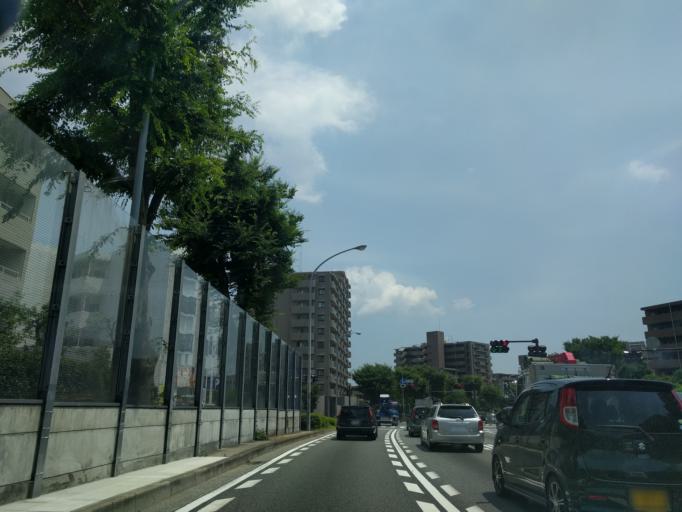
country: JP
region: Kanagawa
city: Yokohama
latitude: 35.4363
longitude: 139.5625
